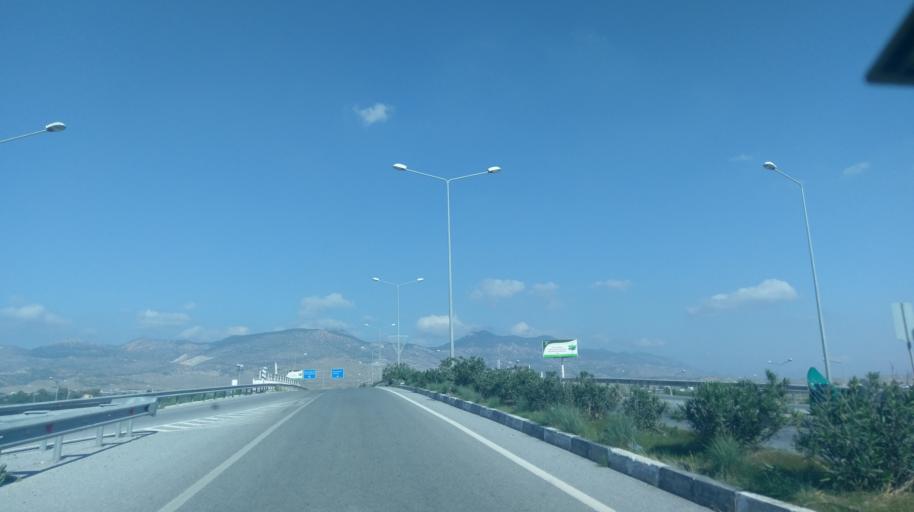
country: CY
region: Lefkosia
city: Geri
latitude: 35.2178
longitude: 33.4973
